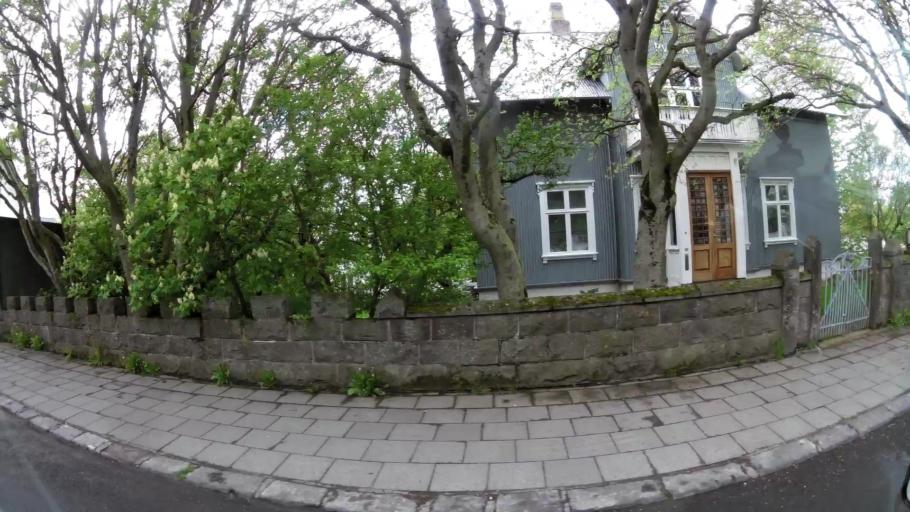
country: IS
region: Capital Region
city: Kopavogur
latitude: 64.1424
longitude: -21.9376
